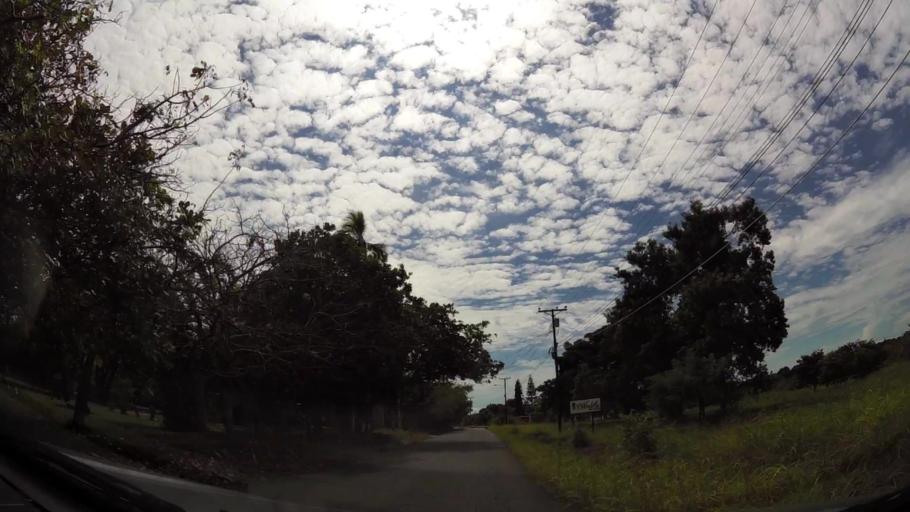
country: PA
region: Panama
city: Nueva Gorgona
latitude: 8.5296
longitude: -79.9164
